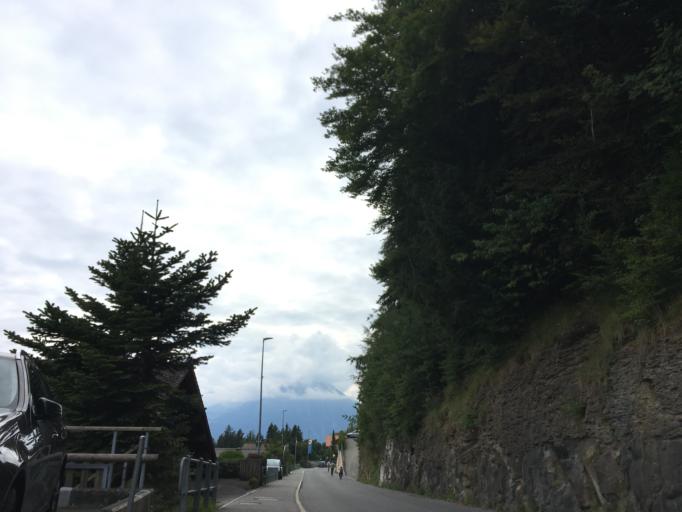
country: CH
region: Bern
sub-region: Interlaken-Oberhasli District
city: Beatenberg
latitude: 46.6909
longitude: 7.7824
